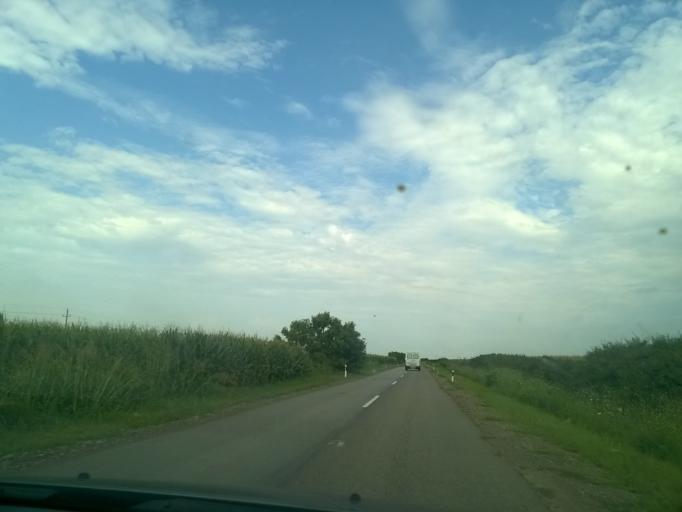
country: RS
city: Stajicevo
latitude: 45.3032
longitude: 20.4866
